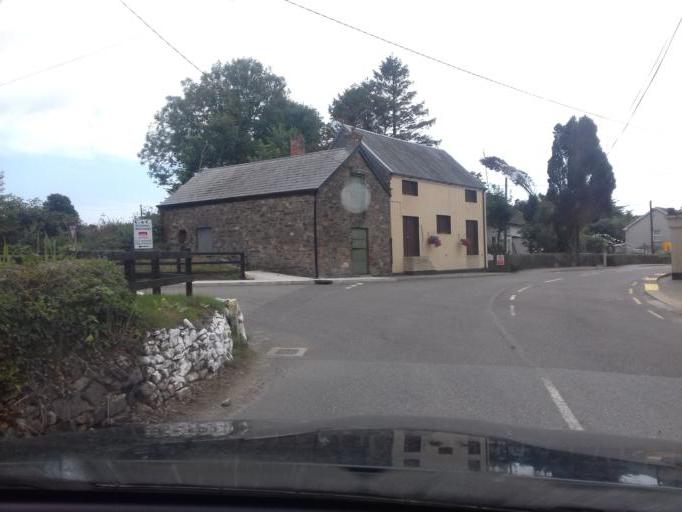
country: IE
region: Leinster
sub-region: Loch Garman
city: Castlebridge
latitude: 52.4132
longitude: -6.4090
